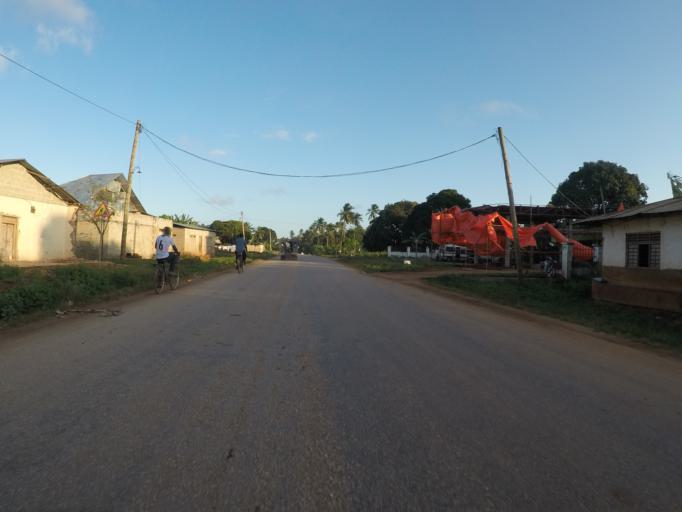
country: TZ
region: Zanzibar North
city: Gamba
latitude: -5.8885
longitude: 39.2881
